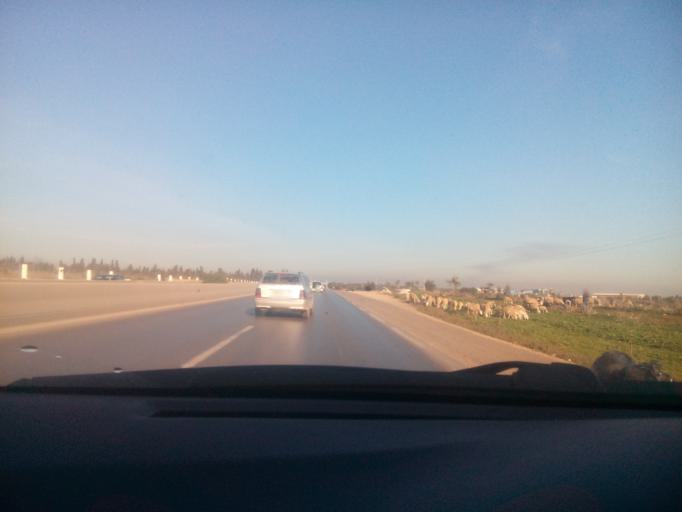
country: DZ
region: Oran
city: Bir el Djir
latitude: 35.7432
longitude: -0.5004
